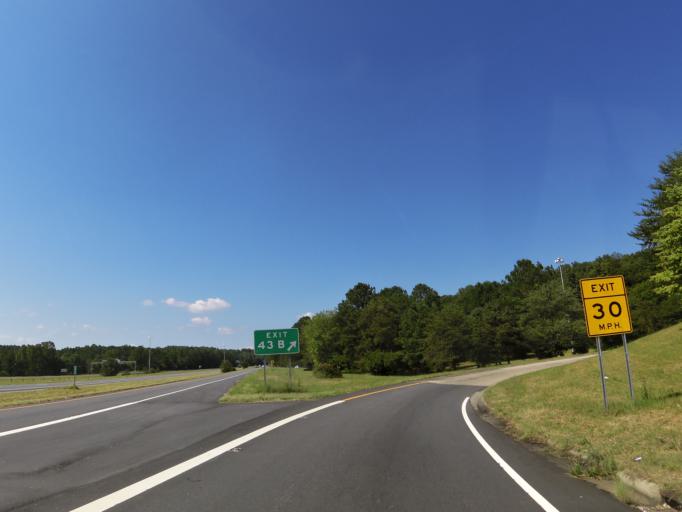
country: US
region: North Carolina
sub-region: Catawba County
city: Hickory
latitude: 35.7093
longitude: -81.3534
